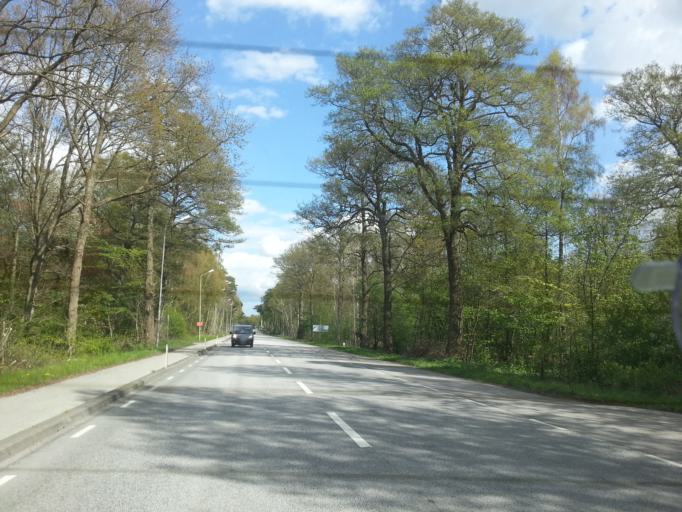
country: SE
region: Skane
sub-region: Ystads Kommun
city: Ystad
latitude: 55.4318
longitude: 13.8590
